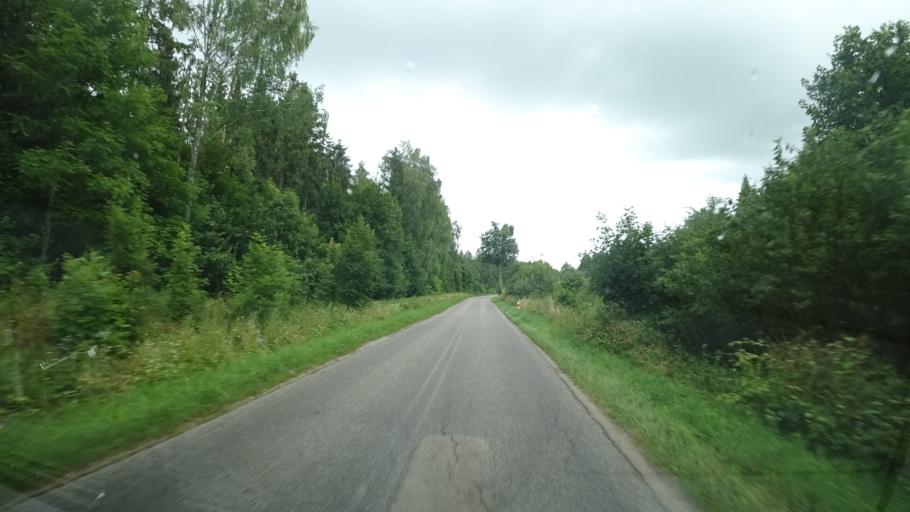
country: PL
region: Warmian-Masurian Voivodeship
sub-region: Powiat goldapski
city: Goldap
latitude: 54.3089
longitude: 22.3871
